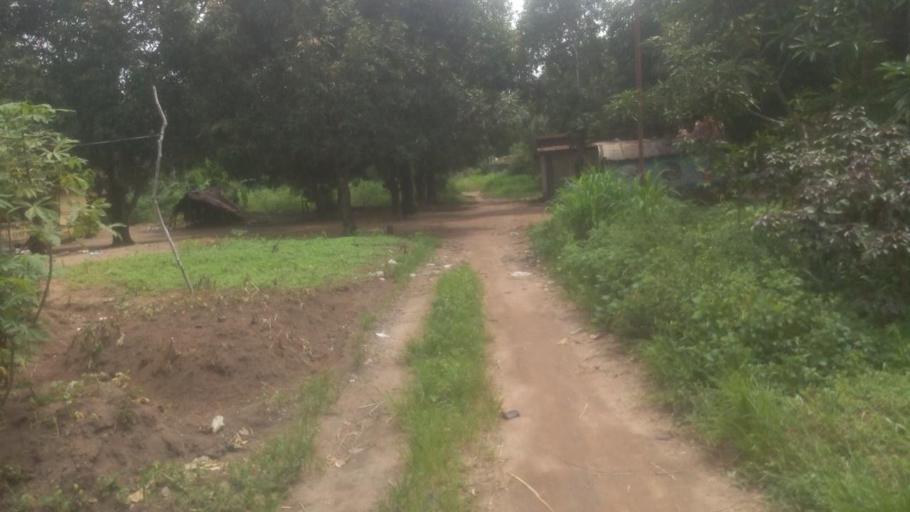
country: SL
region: Northern Province
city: Masoyila
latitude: 8.5474
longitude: -13.1590
